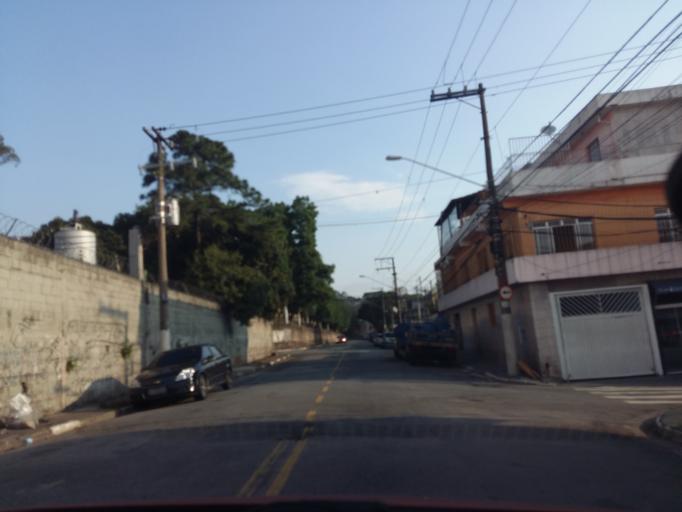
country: BR
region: Sao Paulo
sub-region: Diadema
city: Diadema
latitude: -23.6334
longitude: -46.6254
